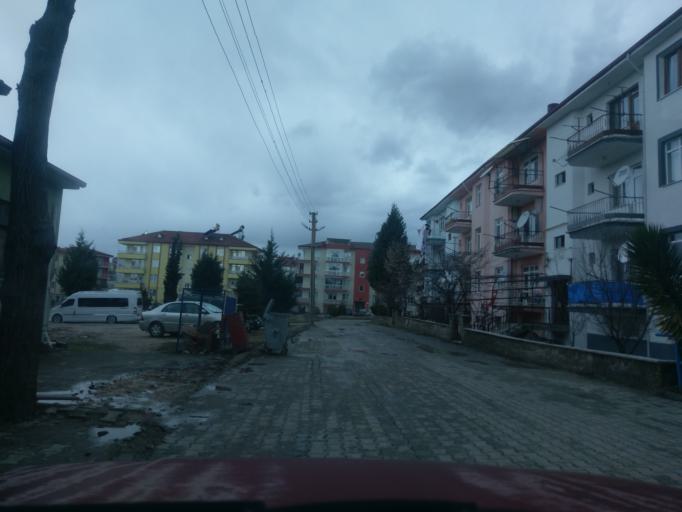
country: TR
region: Kuetahya
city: Gediz
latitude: 38.9940
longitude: 29.3841
